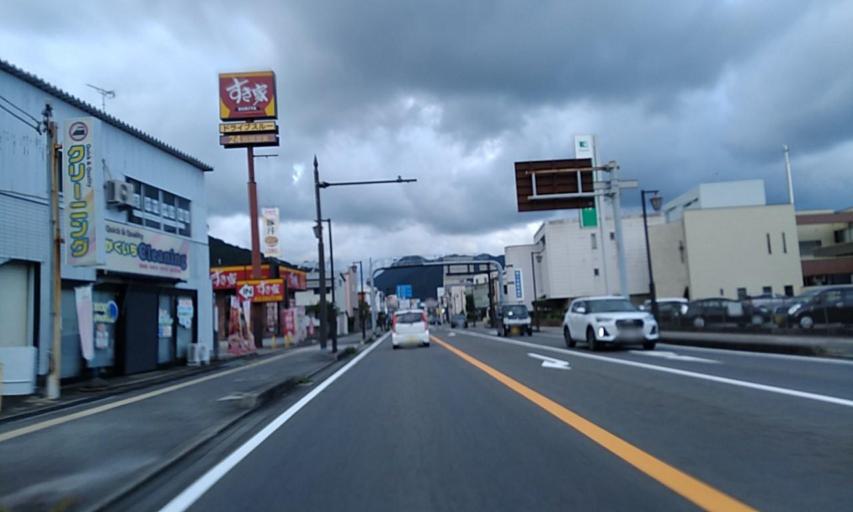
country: JP
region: Wakayama
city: Shingu
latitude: 33.7194
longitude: 135.9867
